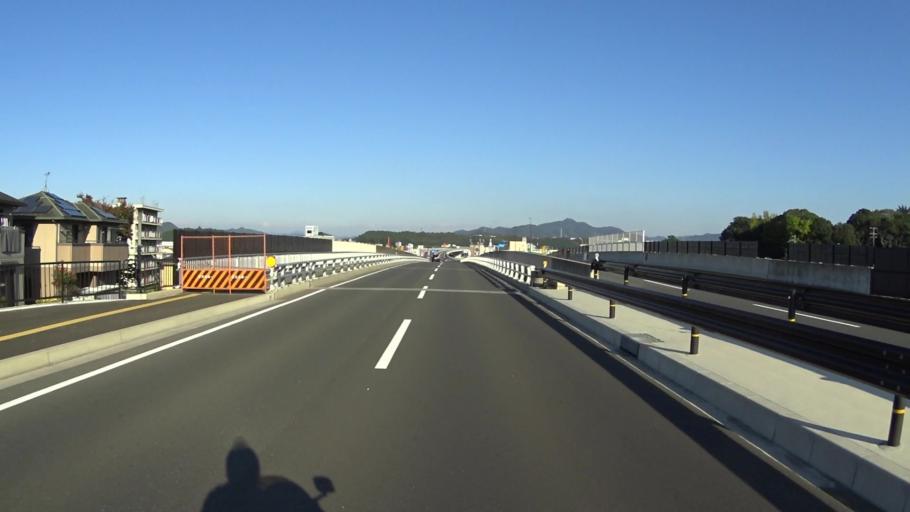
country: JP
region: Kyoto
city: Fukuchiyama
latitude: 35.2902
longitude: 135.1297
